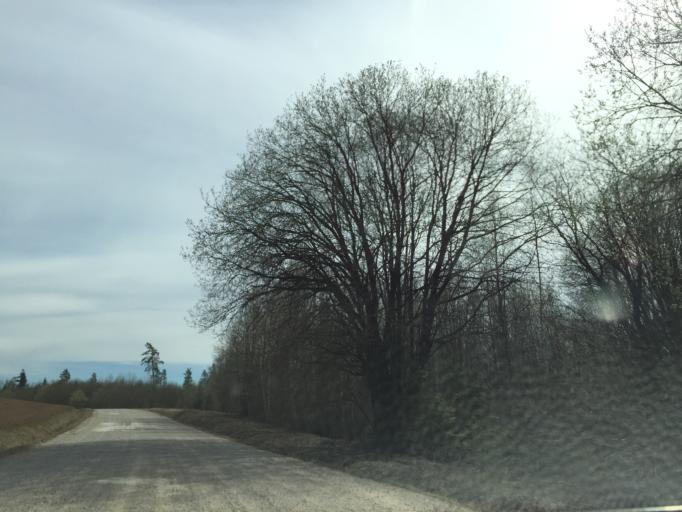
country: LV
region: Valkas Rajons
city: Valka
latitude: 57.8064
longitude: 25.9417
